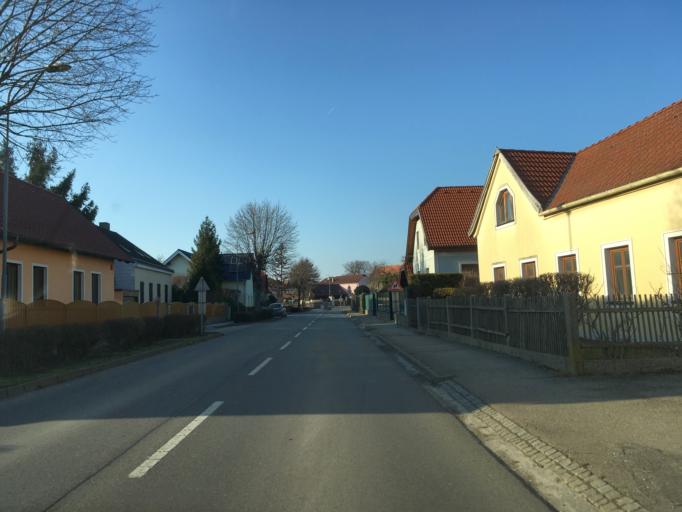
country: AT
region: Lower Austria
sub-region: Politischer Bezirk Tulln
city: Wordern
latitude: 48.3275
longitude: 16.1791
